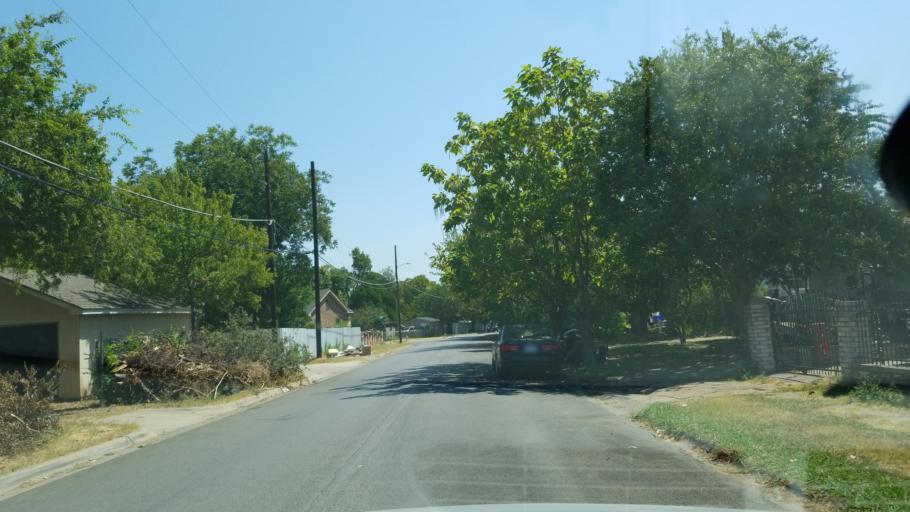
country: US
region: Texas
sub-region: Dallas County
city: Cockrell Hill
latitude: 32.7450
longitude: -96.8850
